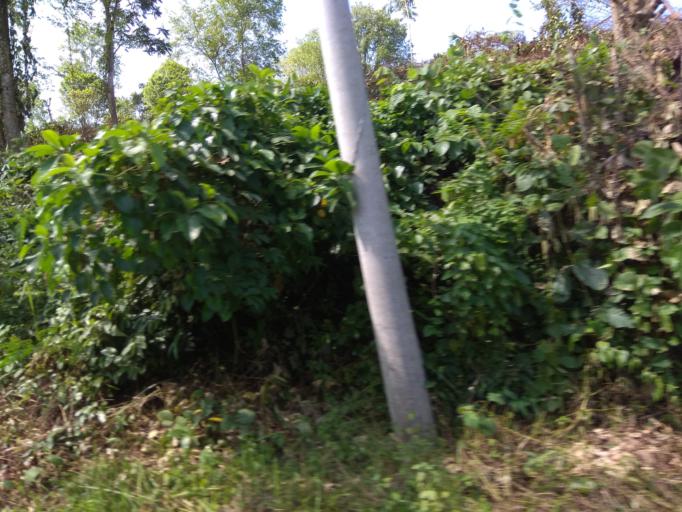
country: BD
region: Chittagong
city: Khagrachhari
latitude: 23.0356
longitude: 92.0062
